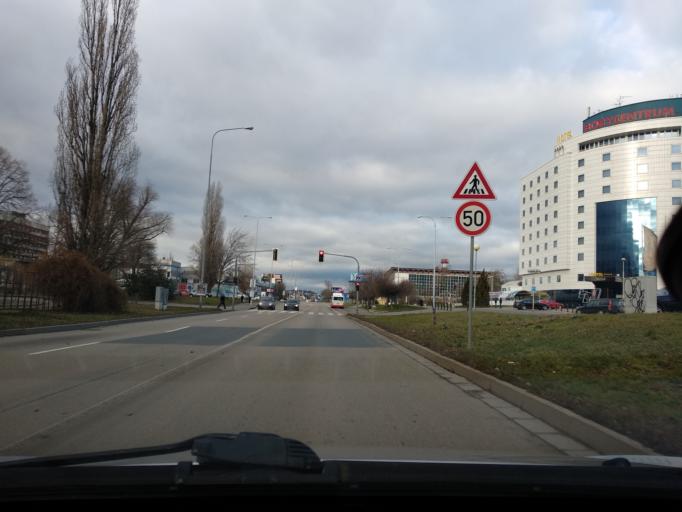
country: CZ
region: South Moravian
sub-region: Mesto Brno
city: Brno
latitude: 49.2112
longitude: 16.6077
